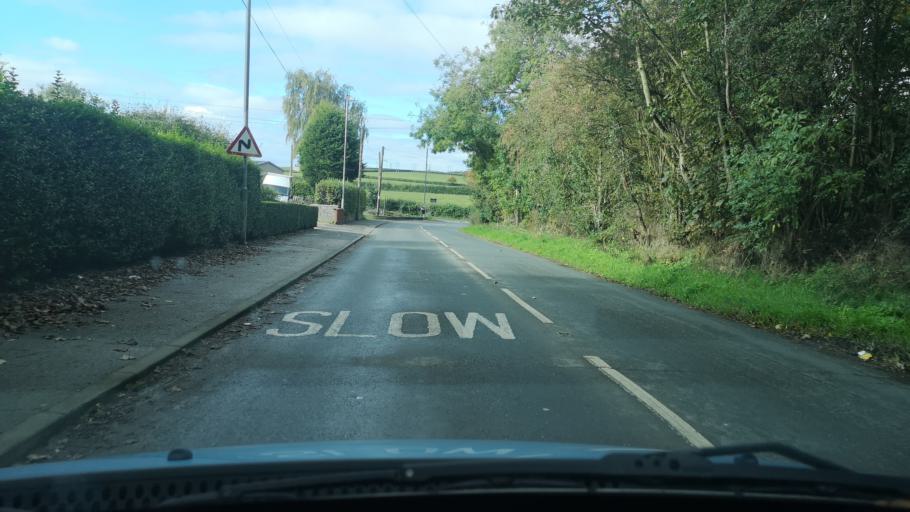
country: GB
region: England
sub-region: City and Borough of Wakefield
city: Sharlston
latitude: 53.6866
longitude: -1.3885
